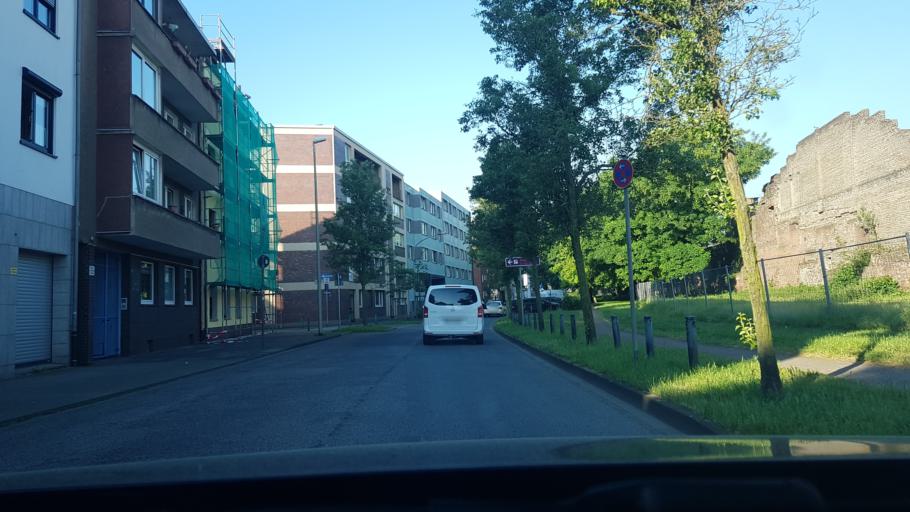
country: DE
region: North Rhine-Westphalia
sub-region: Regierungsbezirk Dusseldorf
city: Duisburg
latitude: 51.4350
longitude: 6.7573
